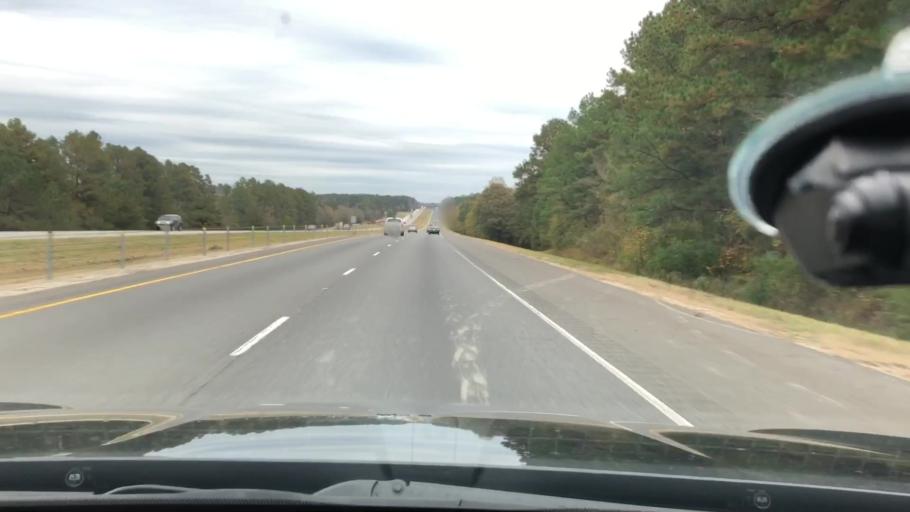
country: US
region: Arkansas
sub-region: Hot Spring County
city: Malvern
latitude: 34.3229
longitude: -92.9298
